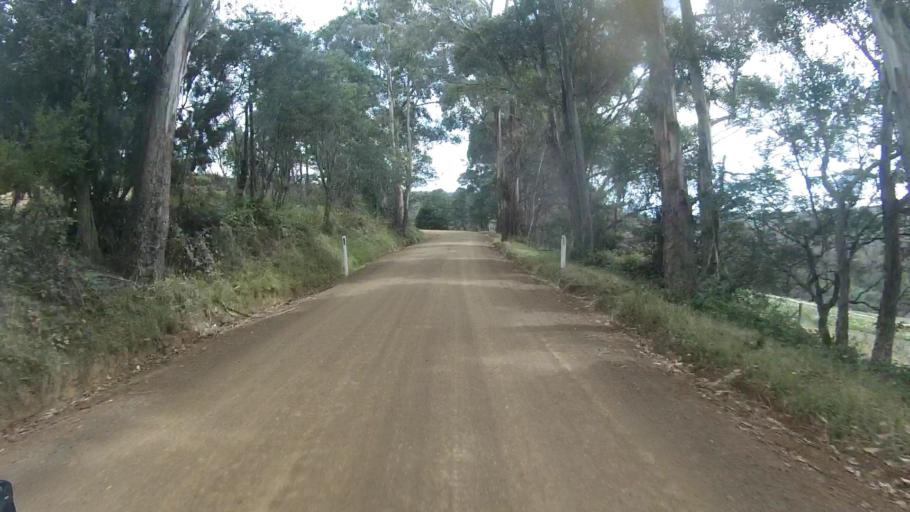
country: AU
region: Tasmania
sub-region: Sorell
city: Sorell
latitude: -42.7312
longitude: 147.7607
